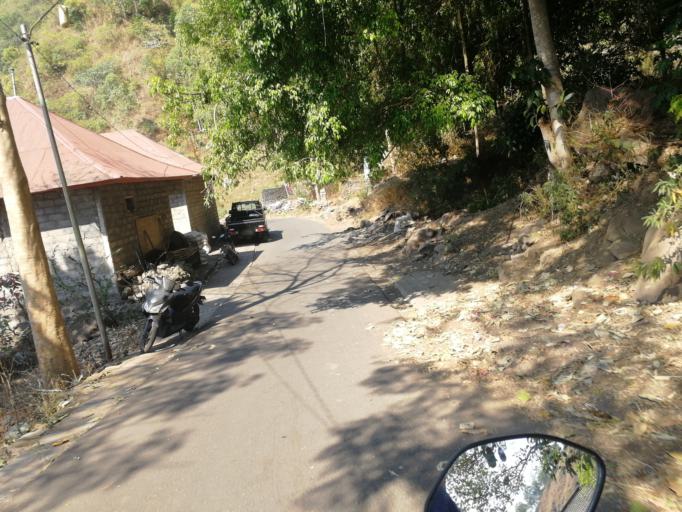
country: ID
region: Bali
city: Banjar Trunyan
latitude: -8.2535
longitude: 115.4264
